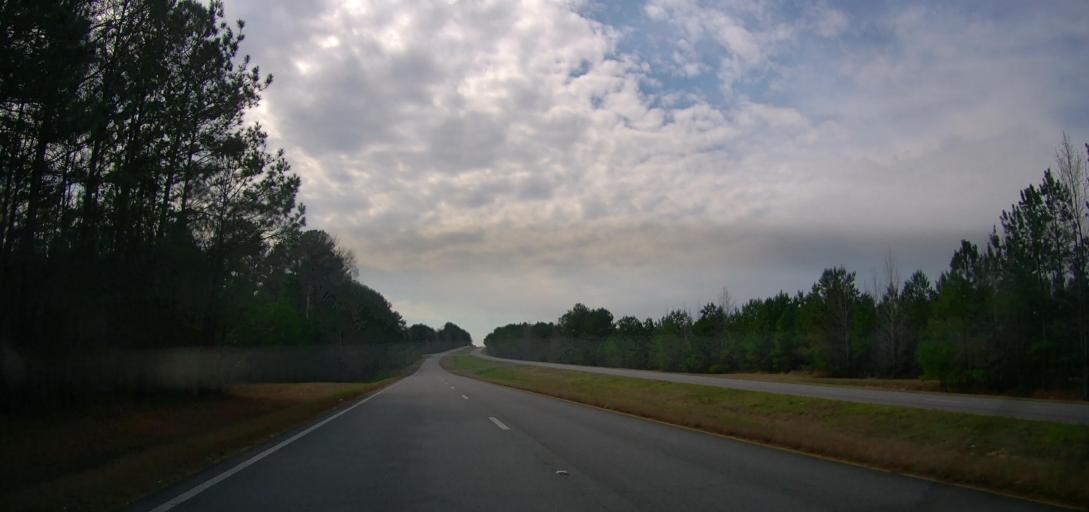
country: US
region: Alabama
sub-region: Marion County
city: Winfield
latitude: 33.9302
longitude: -87.6865
